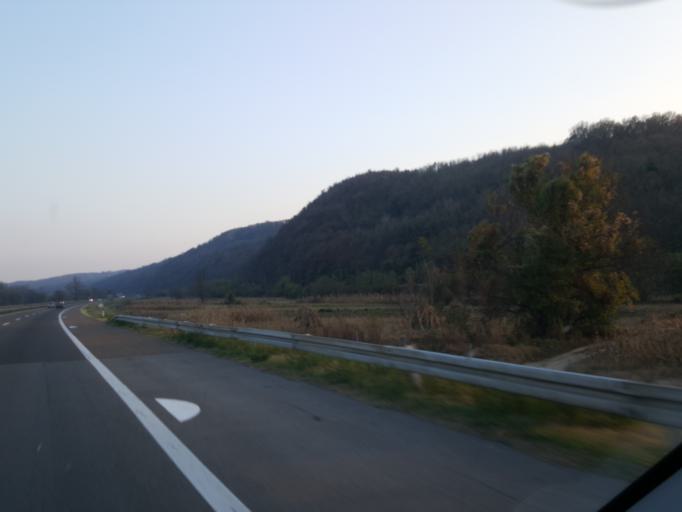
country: RS
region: Central Serbia
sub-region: Pomoravski Okrug
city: Jagodina
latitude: 44.0811
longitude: 21.1874
